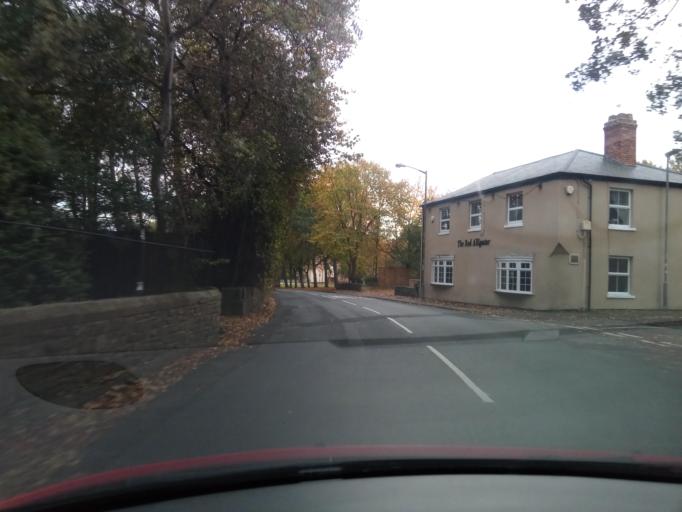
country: GB
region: England
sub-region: County Durham
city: Bishop Auckland
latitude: 54.6509
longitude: -1.6631
